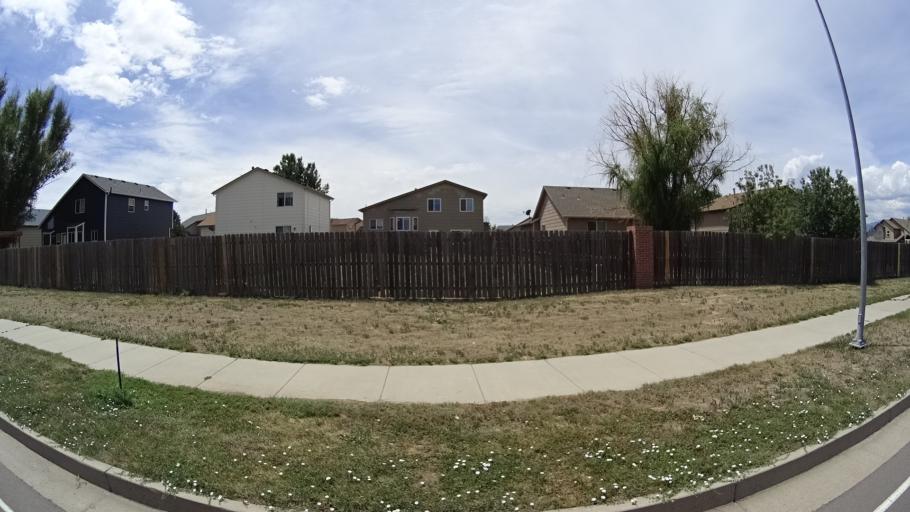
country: US
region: Colorado
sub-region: El Paso County
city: Fountain
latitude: 38.6714
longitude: -104.6840
